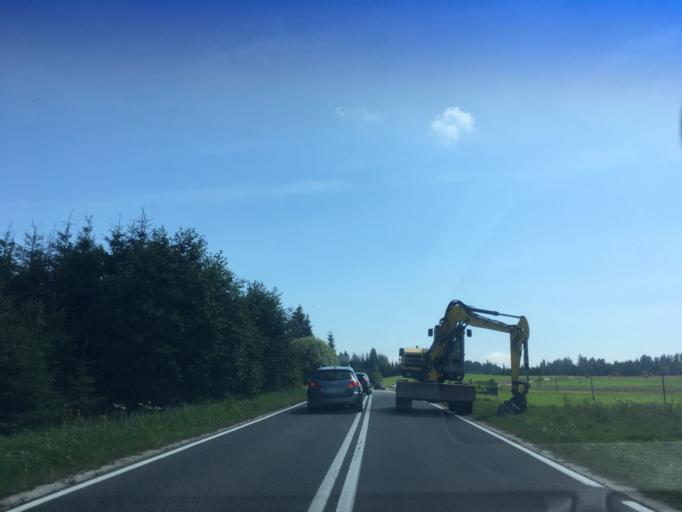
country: PL
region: Lesser Poland Voivodeship
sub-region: Powiat nowotarski
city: Maniowy
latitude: 49.4333
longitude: 20.2562
